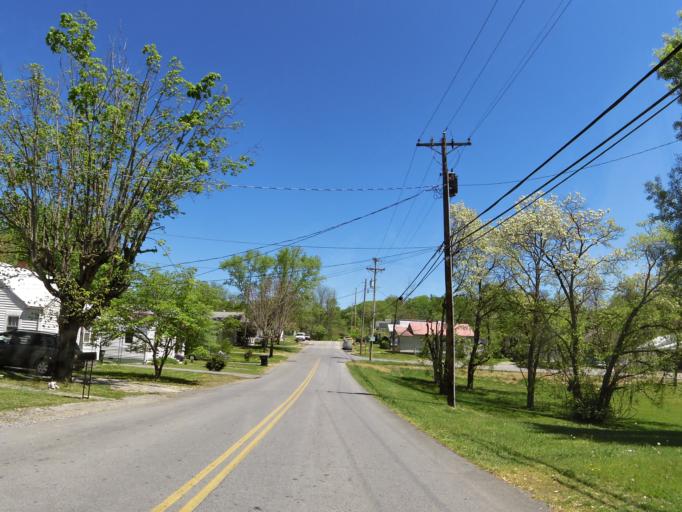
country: US
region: Tennessee
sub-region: Greene County
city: Greeneville
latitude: 36.1559
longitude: -82.8406
